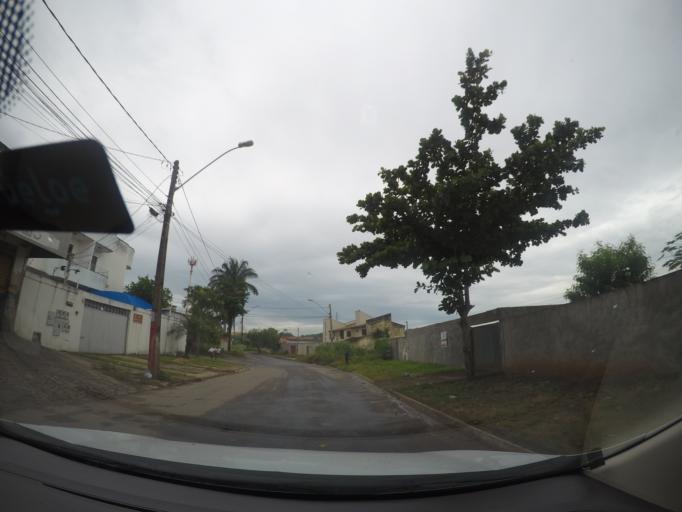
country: BR
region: Goias
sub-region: Goiania
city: Goiania
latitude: -16.6474
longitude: -49.2633
